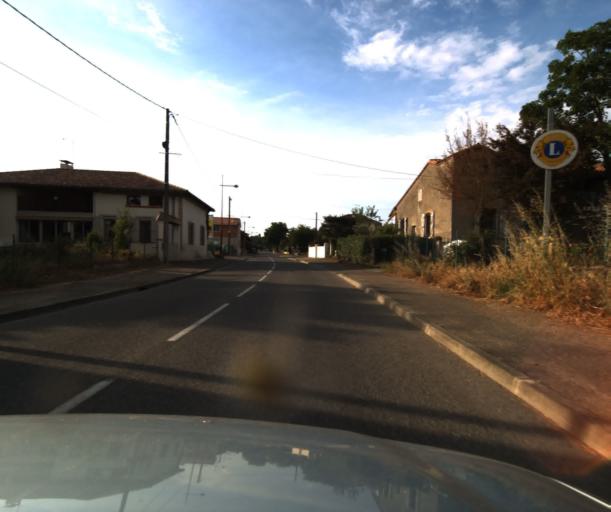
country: FR
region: Midi-Pyrenees
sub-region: Departement du Tarn-et-Garonne
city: Castelsarrasin
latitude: 44.0326
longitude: 1.1069
